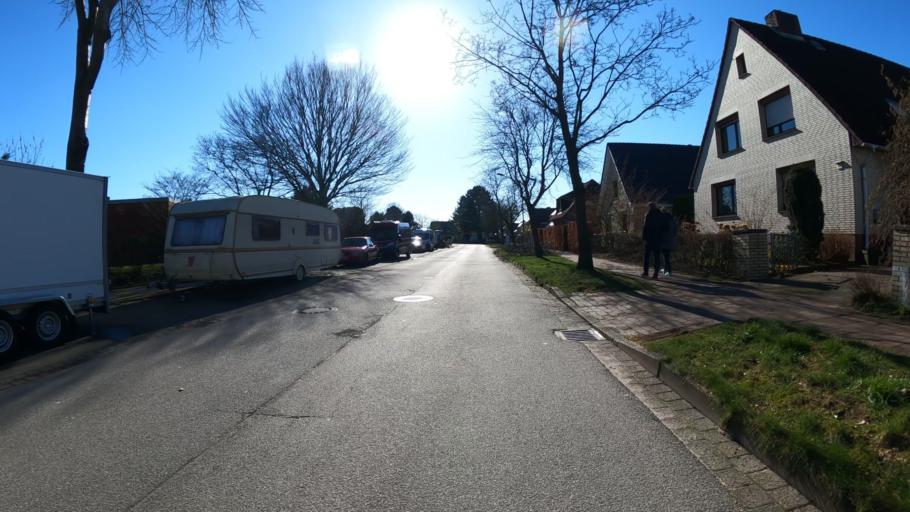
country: DE
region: Schleswig-Holstein
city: Pinneberg
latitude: 53.6757
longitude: 9.7890
